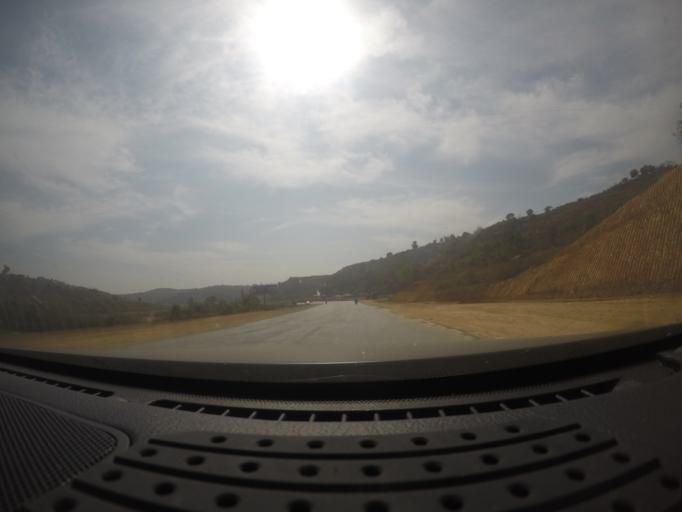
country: MM
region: Shan
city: Taunggyi
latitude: 20.6472
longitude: 96.6000
